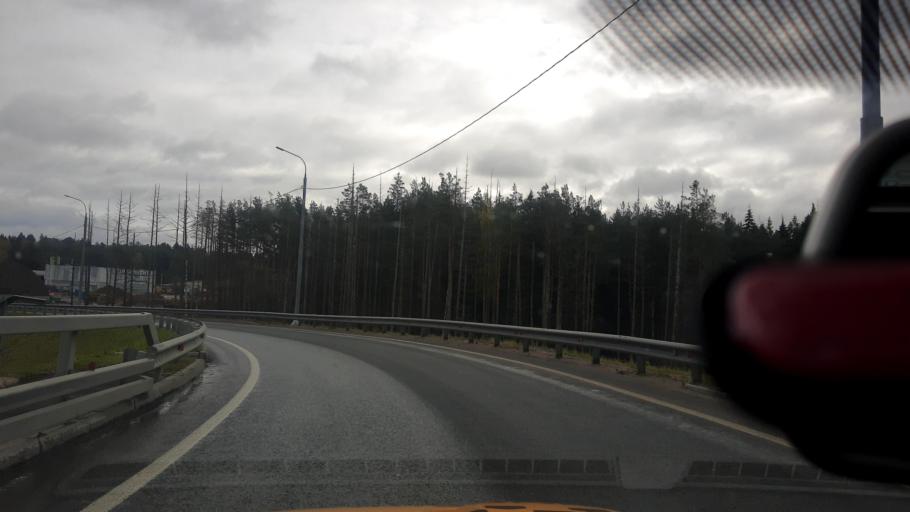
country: RU
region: Moskovskaya
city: Golitsyno
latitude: 55.6011
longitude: 36.9907
